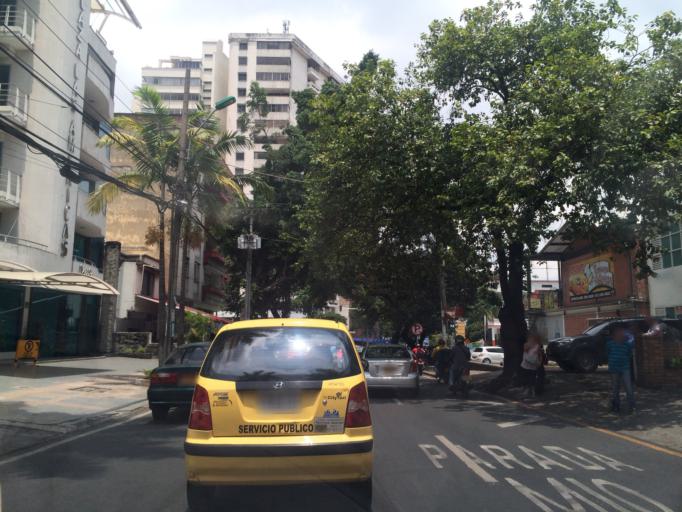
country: CO
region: Valle del Cauca
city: Cali
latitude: 3.4613
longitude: -76.5280
